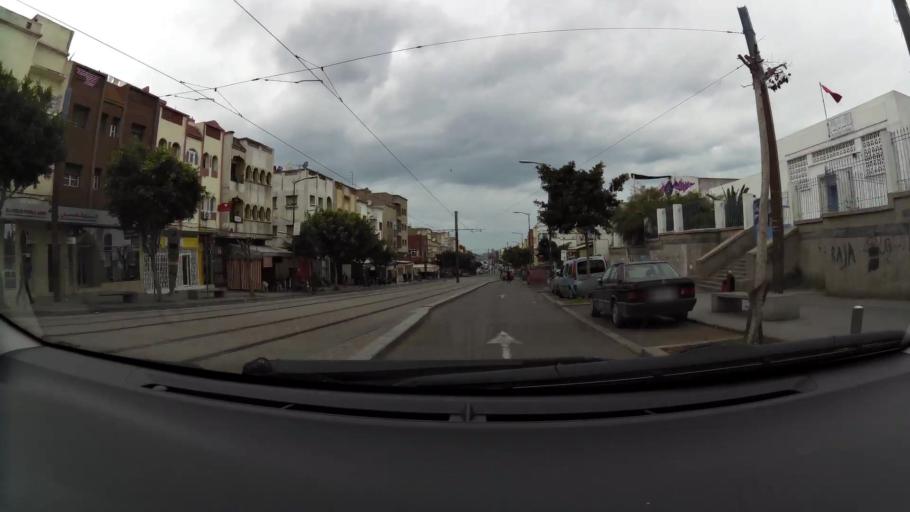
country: MA
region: Grand Casablanca
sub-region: Casablanca
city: Casablanca
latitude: 33.5895
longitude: -7.5680
